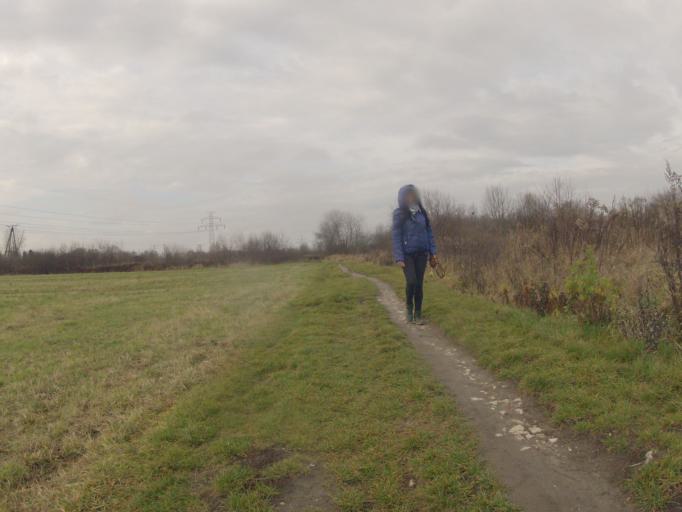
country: PL
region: Lesser Poland Voivodeship
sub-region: Powiat krakowski
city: Rzaska
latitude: 50.0767
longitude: 19.8643
